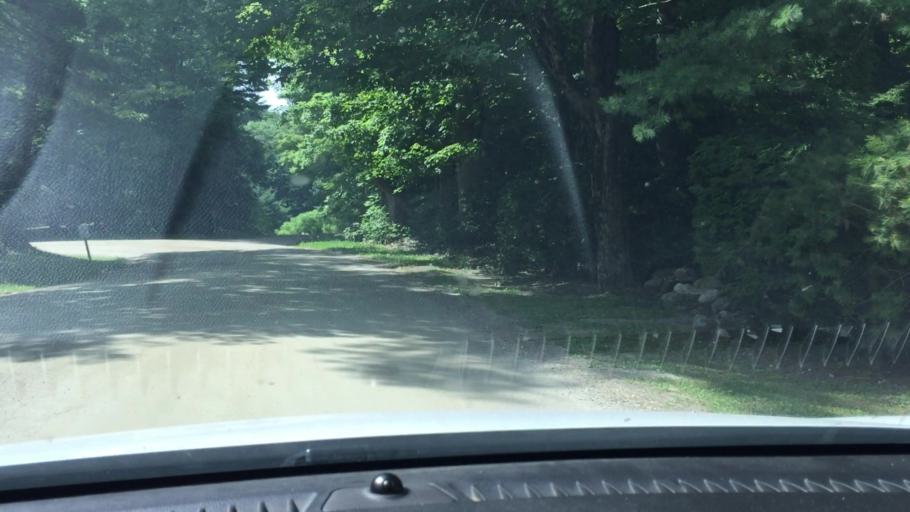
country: US
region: Massachusetts
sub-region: Berkshire County
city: Otis
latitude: 42.1866
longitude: -73.0949
